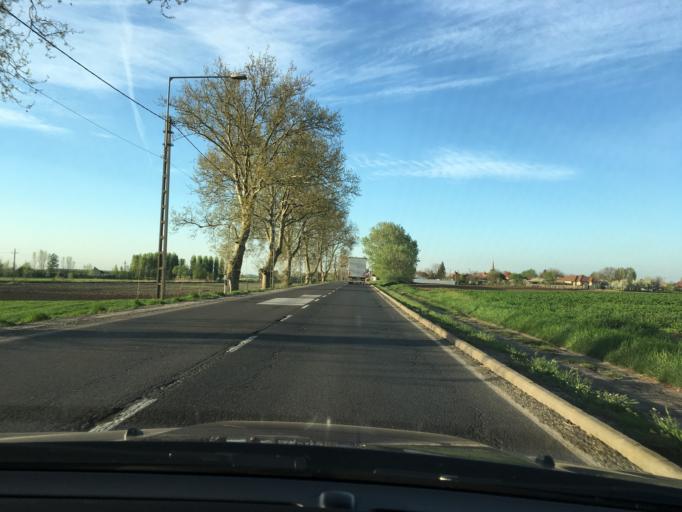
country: HU
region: Hajdu-Bihar
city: Mikepercs
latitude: 47.4318
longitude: 21.6269
